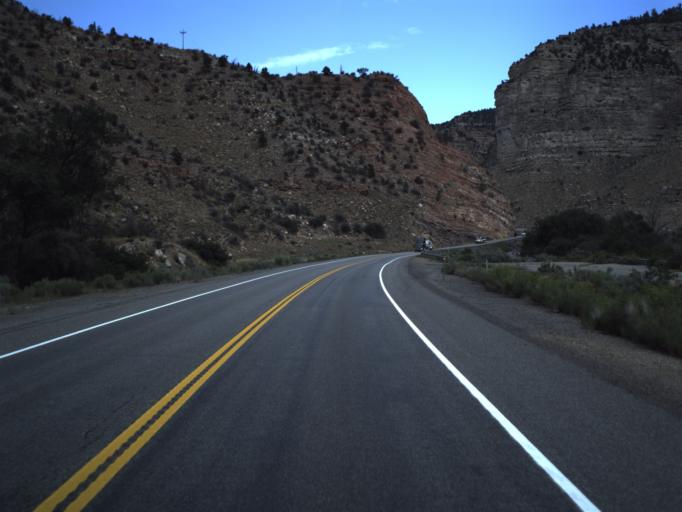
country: US
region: Utah
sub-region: Carbon County
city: Helper
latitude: 39.7348
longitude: -110.8733
